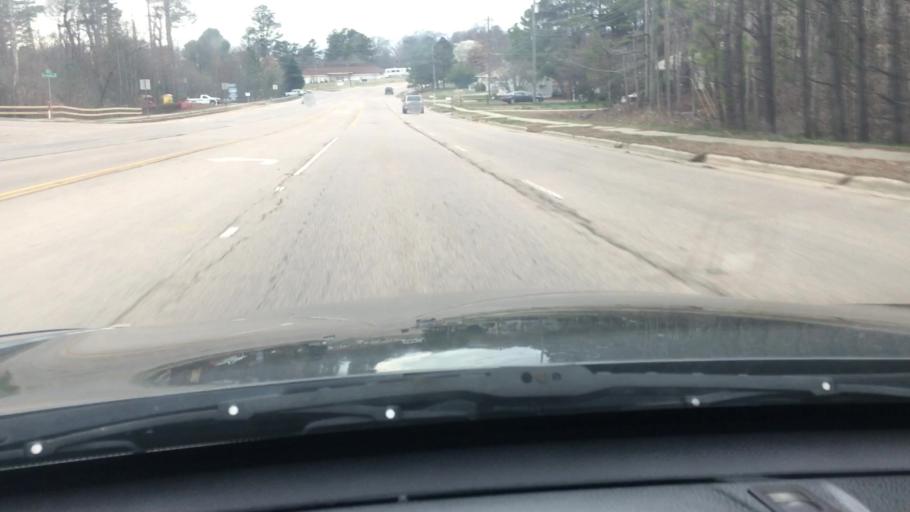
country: US
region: North Carolina
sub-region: Wake County
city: Raleigh
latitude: 35.8305
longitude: -78.5750
